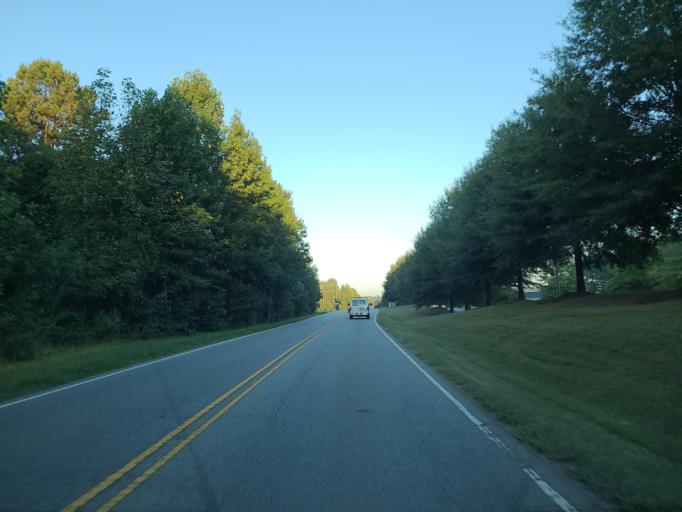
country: US
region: North Carolina
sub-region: Union County
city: Wesley Chapel
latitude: 35.0009
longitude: -80.7064
